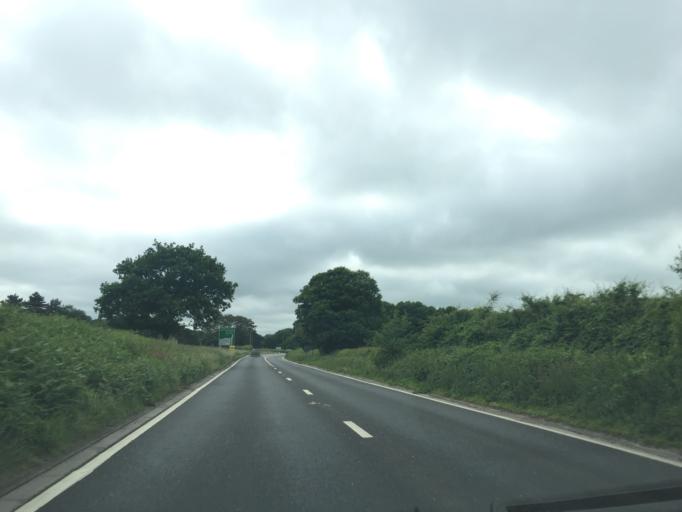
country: GB
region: England
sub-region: Dorset
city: Broadstone
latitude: 50.7856
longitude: -2.0308
